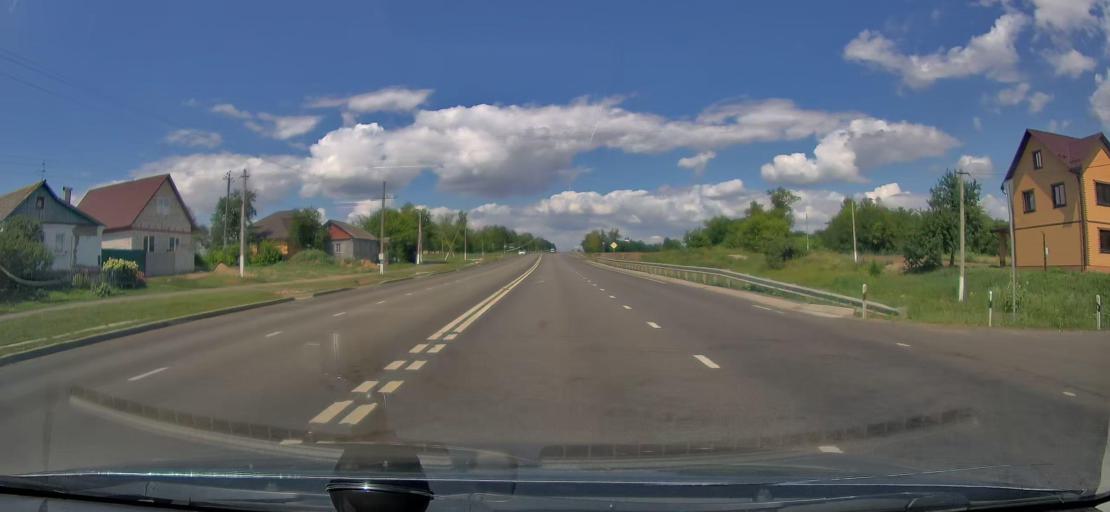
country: RU
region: Kursk
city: Zolotukhino
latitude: 51.9508
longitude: 36.3045
